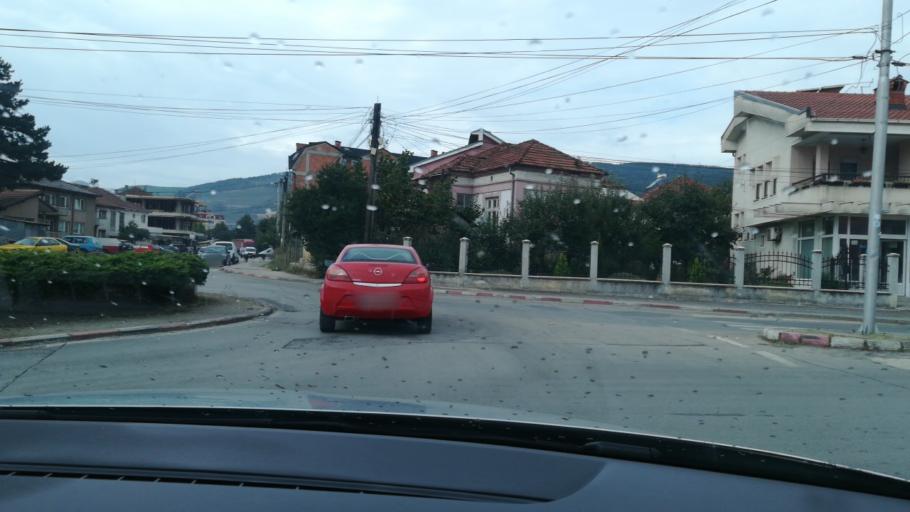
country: MK
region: Kicevo
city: Kicevo
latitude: 41.5091
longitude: 20.9588
